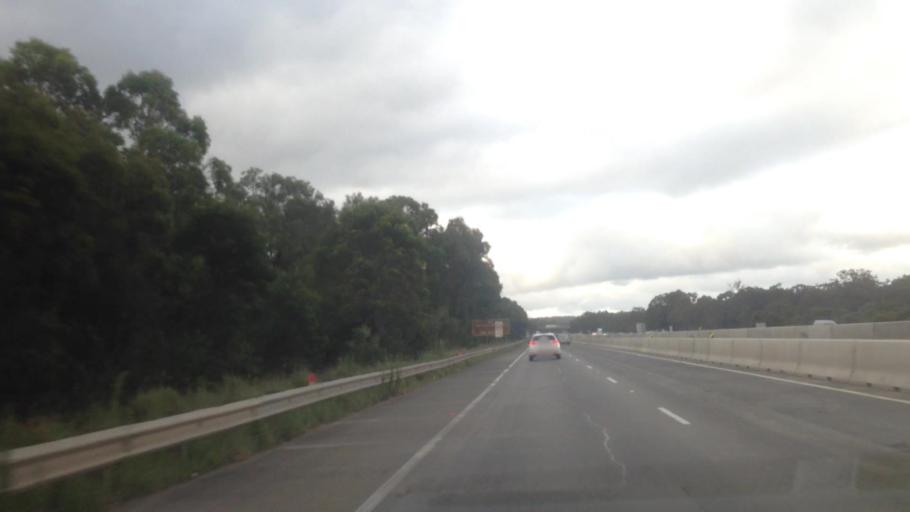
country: AU
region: New South Wales
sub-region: Wyong Shire
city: Jilliby
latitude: -33.2378
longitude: 151.4138
